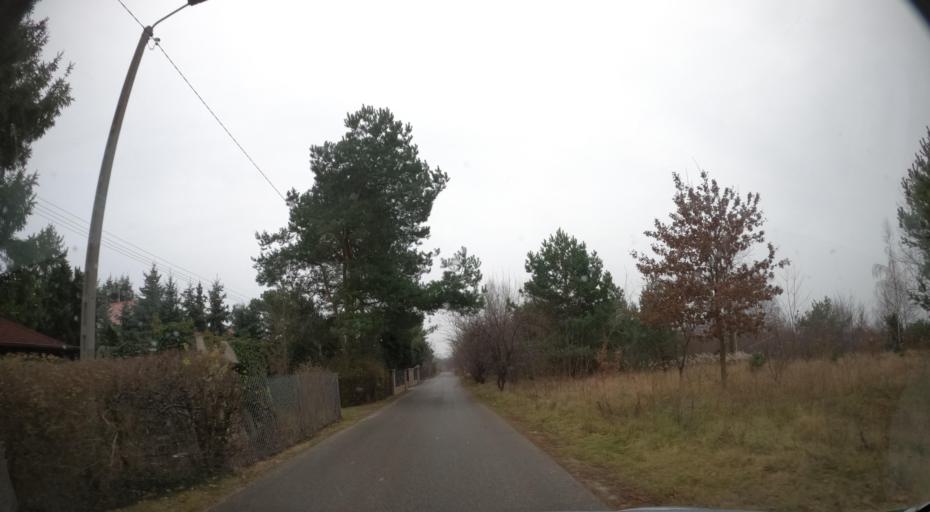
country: PL
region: Masovian Voivodeship
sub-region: Powiat radomski
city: Jastrzebia
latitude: 51.4323
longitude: 21.2292
